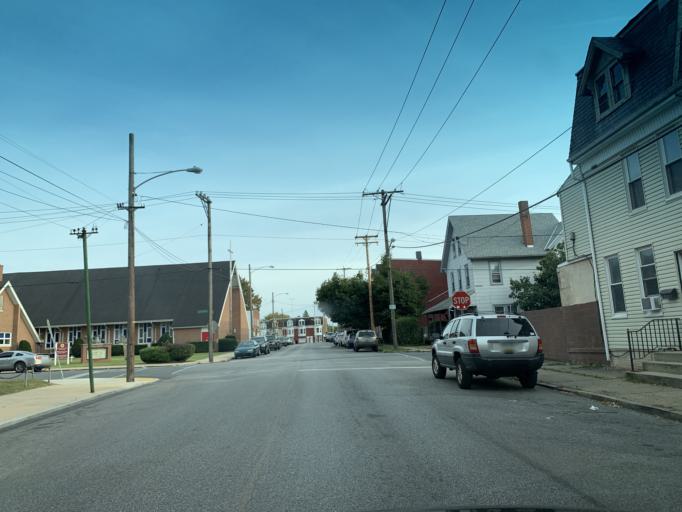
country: US
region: Pennsylvania
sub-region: York County
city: York
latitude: 39.9680
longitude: -76.7353
